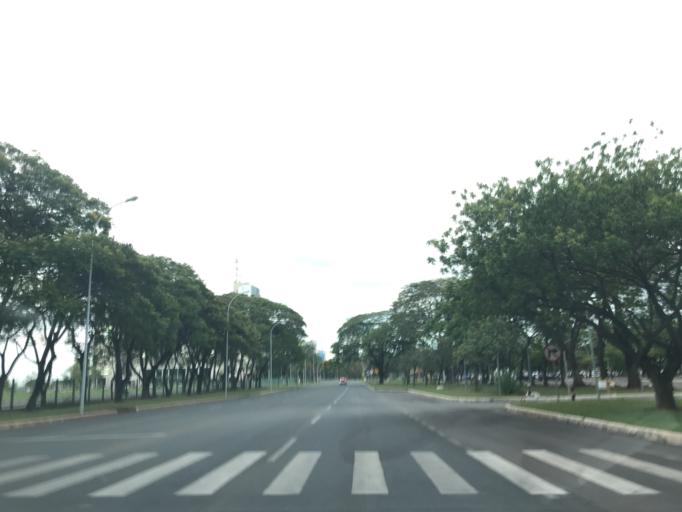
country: BR
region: Federal District
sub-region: Brasilia
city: Brasilia
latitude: -15.7916
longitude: -47.8979
